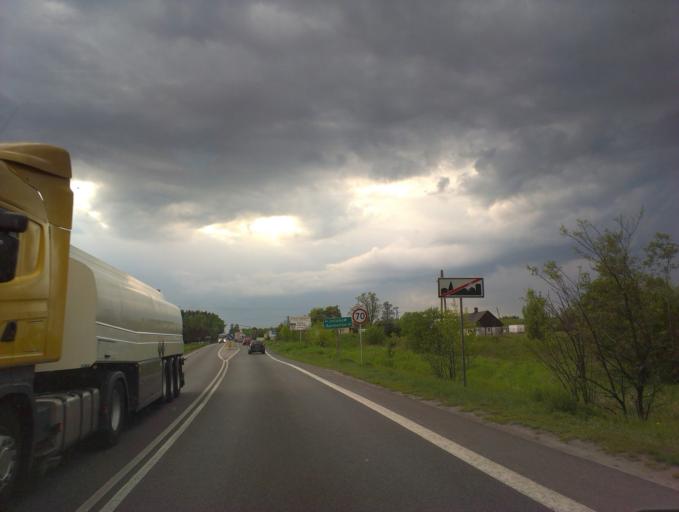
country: PL
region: Masovian Voivodeship
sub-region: Powiat grojecki
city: Pniewy
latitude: 51.8975
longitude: 20.7798
